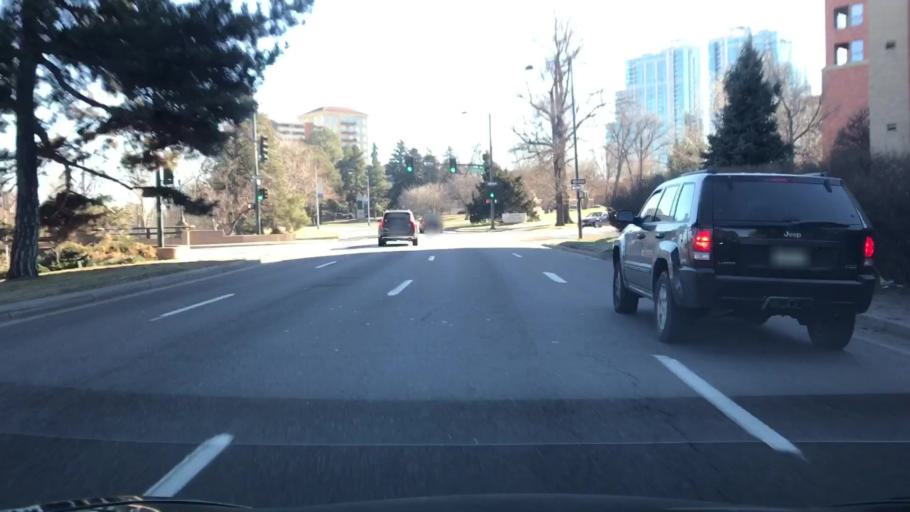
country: US
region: Colorado
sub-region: Denver County
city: Denver
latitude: 39.7197
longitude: -104.9781
